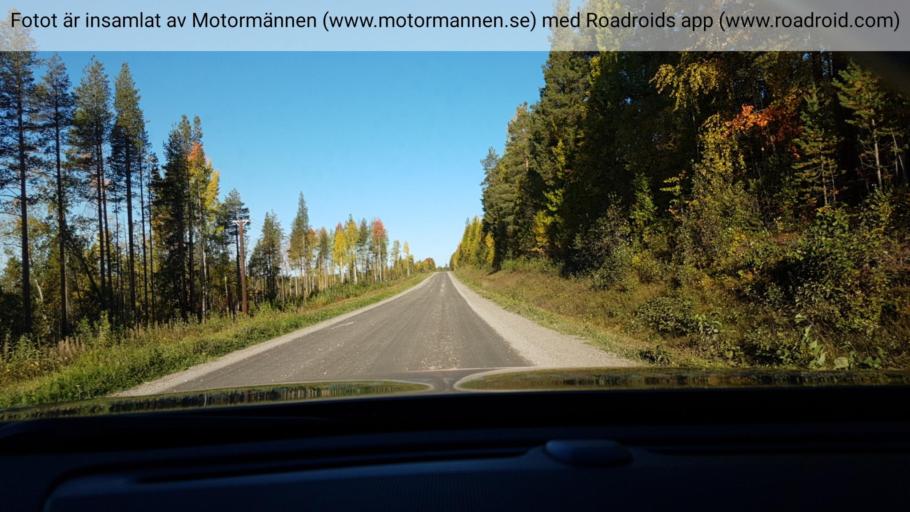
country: SE
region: Norrbotten
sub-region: Alvsbyns Kommun
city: AElvsbyn
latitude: 66.1836
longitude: 21.2158
